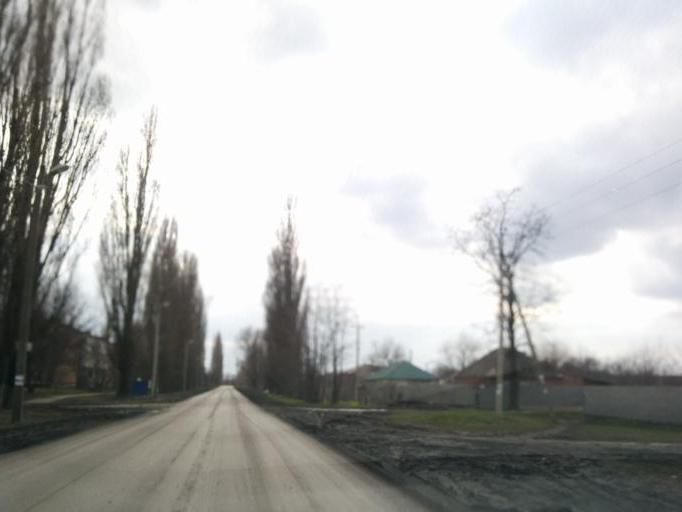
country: RU
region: Rostov
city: Shakhty
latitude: 47.6865
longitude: 40.2879
